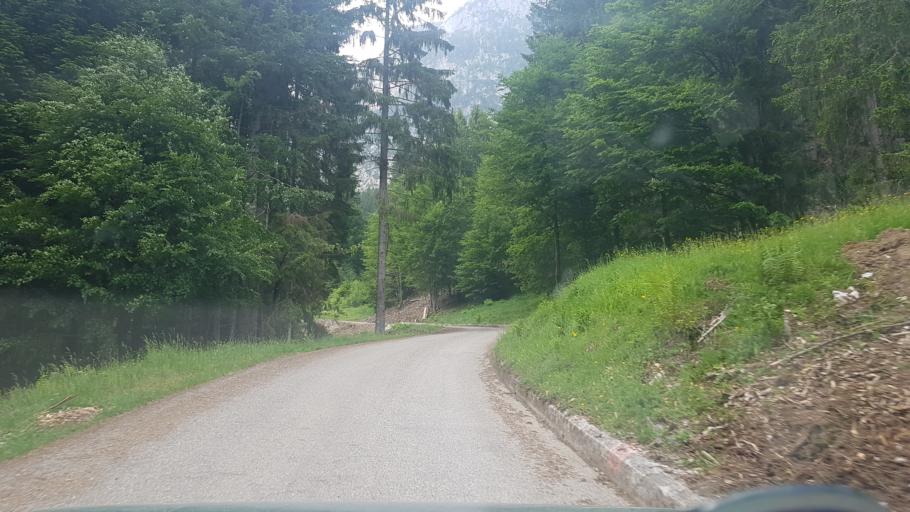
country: IT
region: Friuli Venezia Giulia
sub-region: Provincia di Udine
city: Paularo
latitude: 46.5410
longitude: 13.2049
